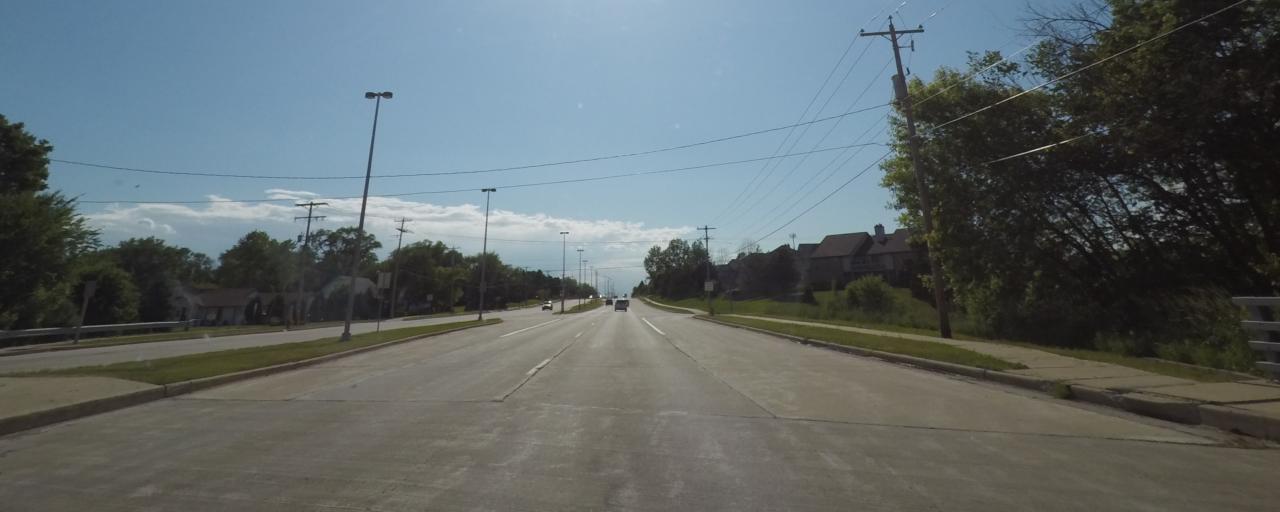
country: US
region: Wisconsin
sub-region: Milwaukee County
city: Greendale
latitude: 42.9163
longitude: -87.9588
